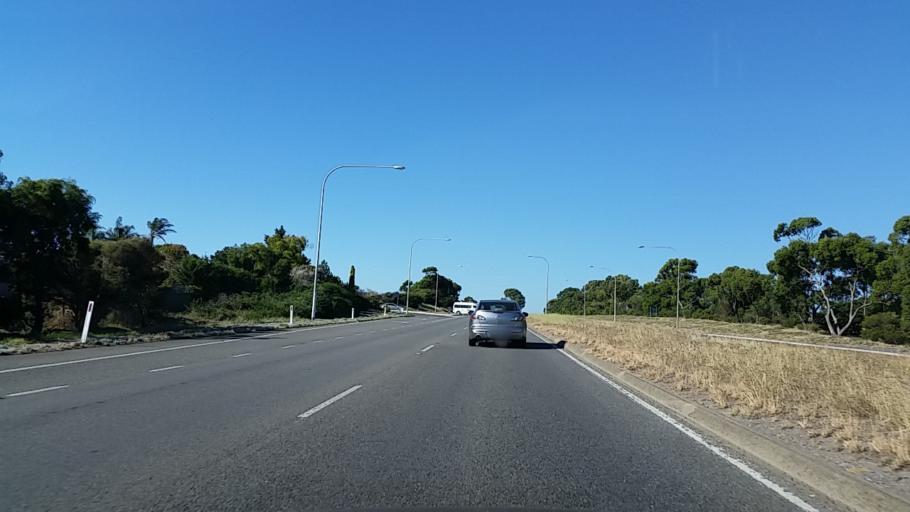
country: AU
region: South Australia
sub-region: Marion
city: Happy Valley
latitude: -35.0707
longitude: 138.5268
